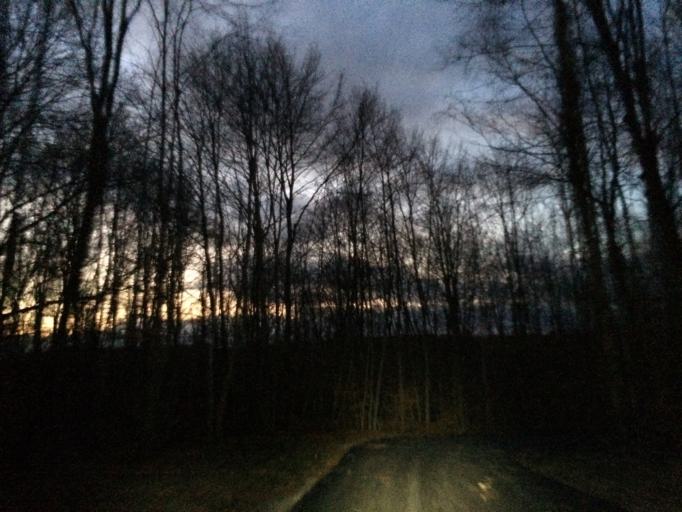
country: FR
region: Picardie
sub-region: Departement de l'Oise
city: Coye-la-Foret
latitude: 49.1537
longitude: 2.4793
